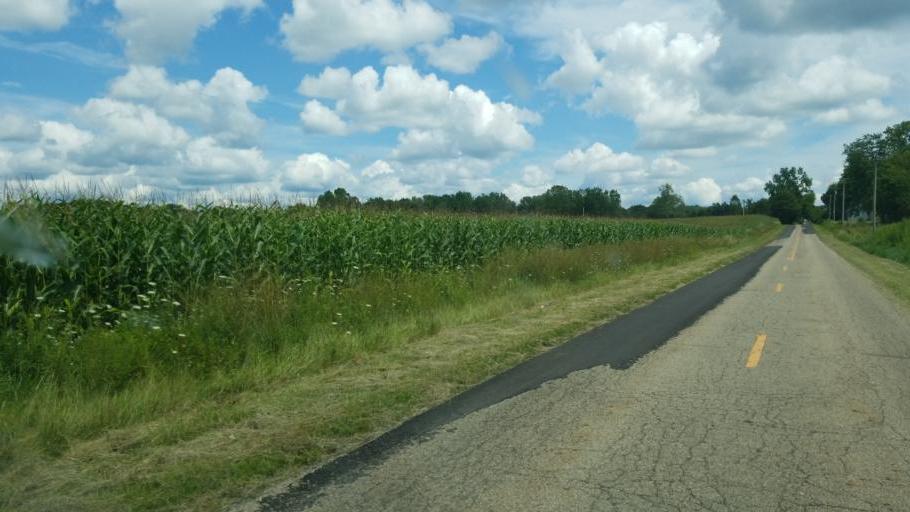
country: US
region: Ohio
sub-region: Knox County
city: Centerburg
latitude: 40.3752
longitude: -82.6363
